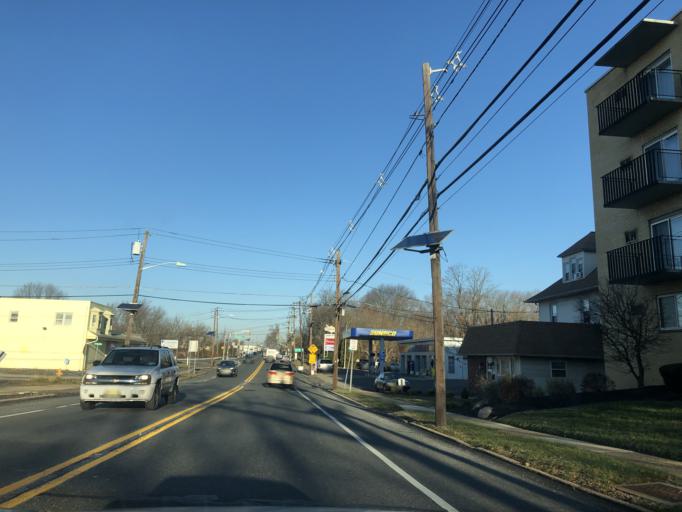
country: US
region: New Jersey
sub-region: Camden County
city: Audubon
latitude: 39.8957
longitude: -75.0703
